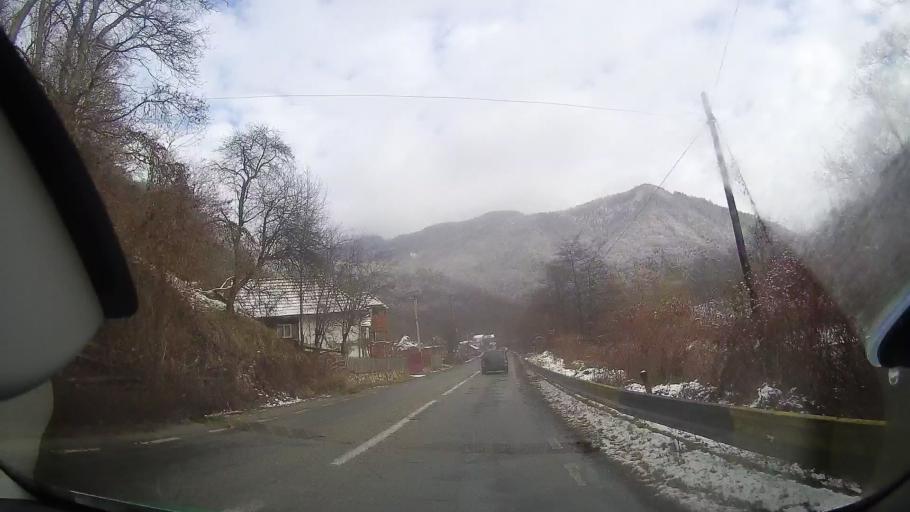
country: RO
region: Alba
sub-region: Oras Baia de Aries
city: Baia de Aries
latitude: 46.4048
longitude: 23.3254
